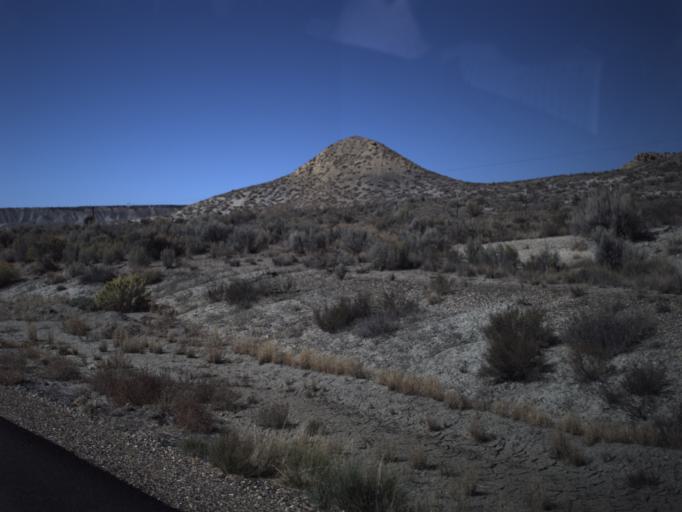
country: US
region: Utah
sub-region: Garfield County
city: Panguitch
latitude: 37.5938
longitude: -111.9386
